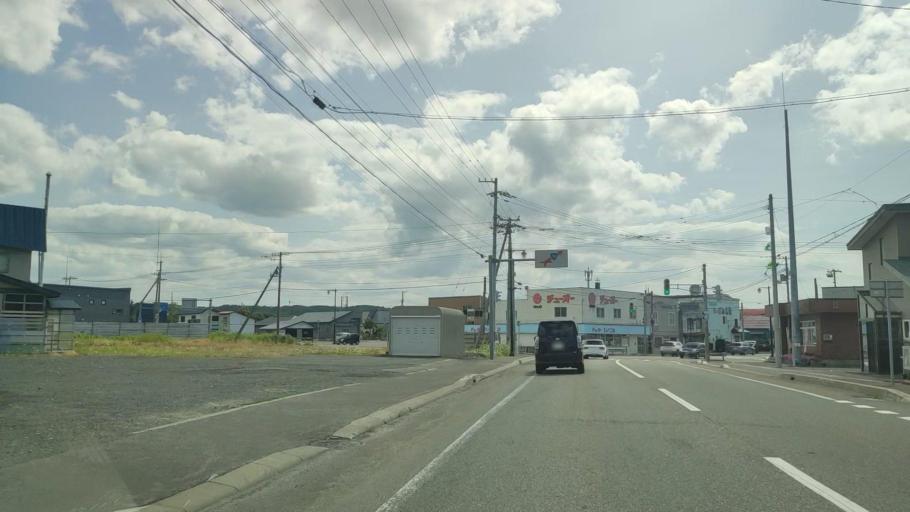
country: JP
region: Hokkaido
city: Makubetsu
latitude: 44.7264
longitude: 141.7992
